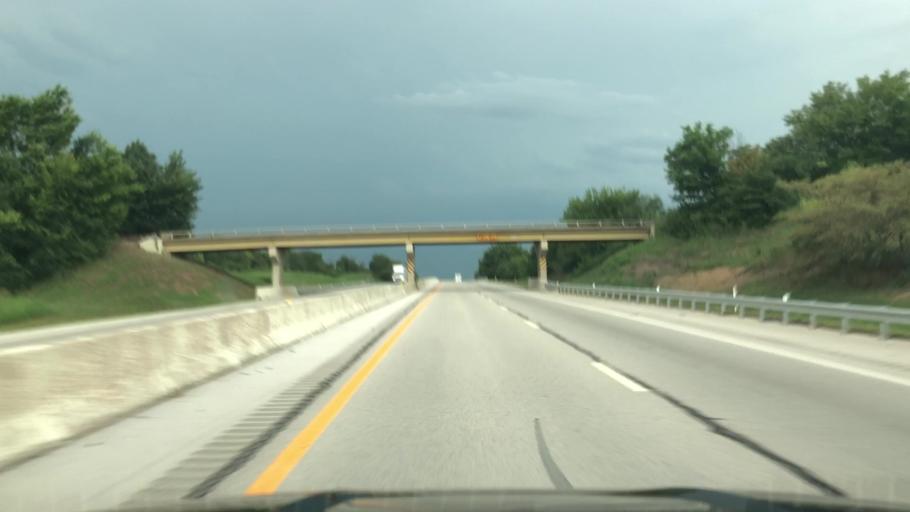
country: US
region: Oklahoma
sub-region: Rogers County
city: Justice
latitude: 36.3426
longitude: -95.4883
